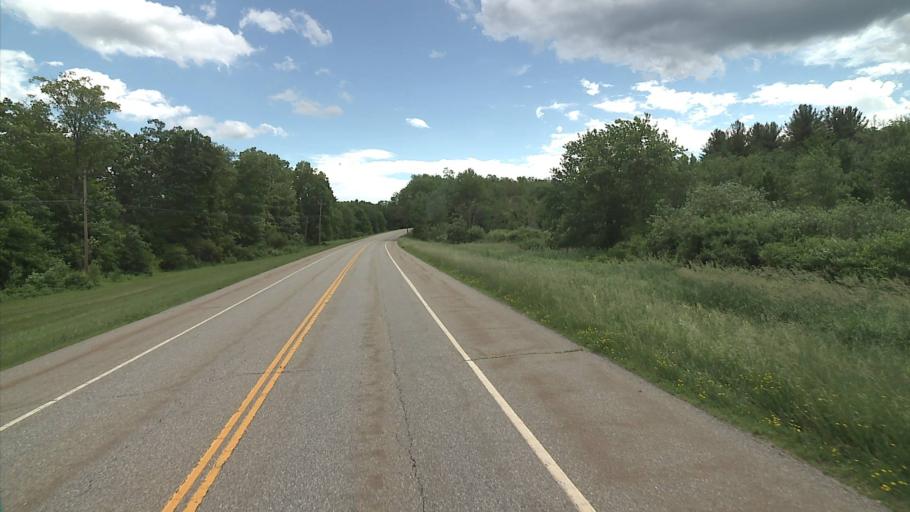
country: US
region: Connecticut
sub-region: Litchfield County
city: Litchfield
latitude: 41.7789
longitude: -73.2045
